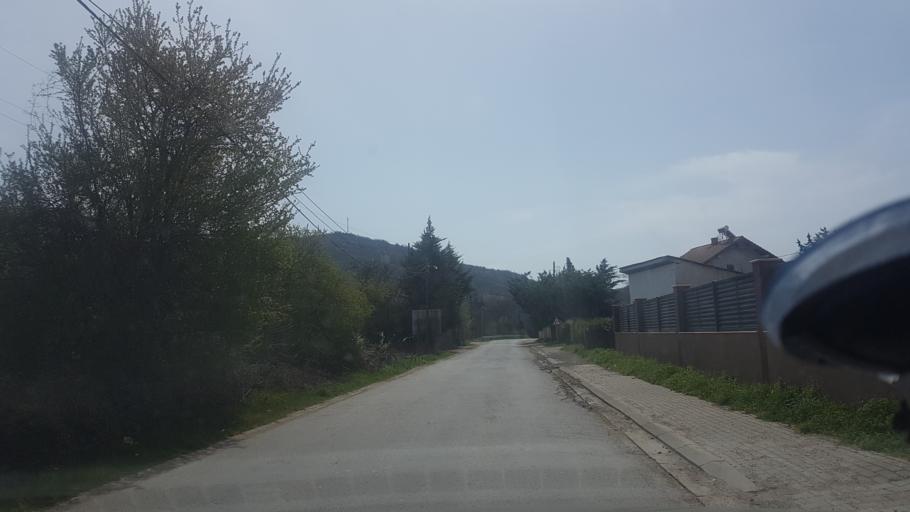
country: MK
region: Zelenikovo
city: Zelenikovo
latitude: 41.8979
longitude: 21.6025
